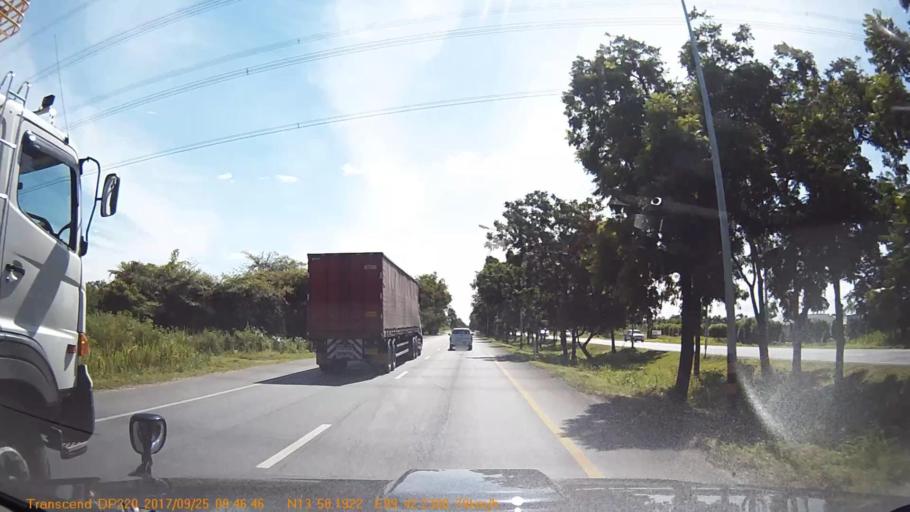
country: TH
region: Kanchanaburi
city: Tha Muang
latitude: 13.9698
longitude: 99.7044
